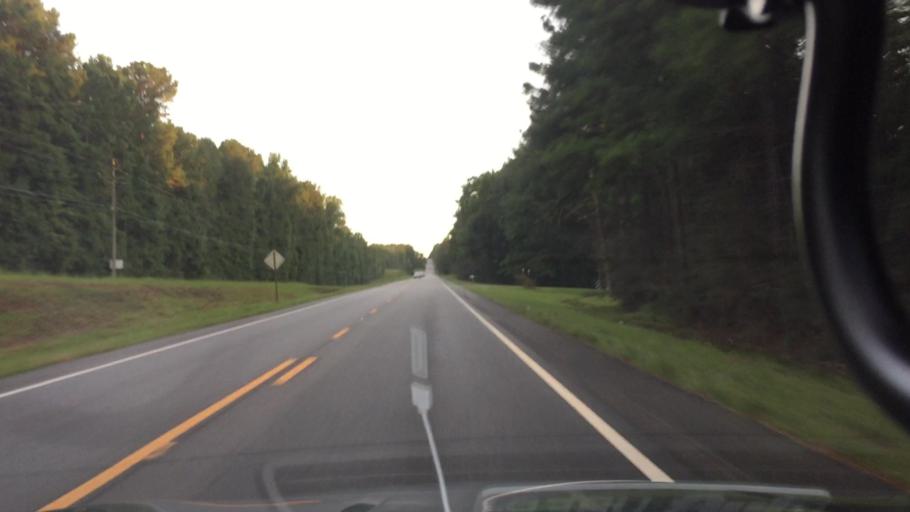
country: US
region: Alabama
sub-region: Coffee County
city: New Brockton
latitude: 31.5315
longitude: -85.9180
